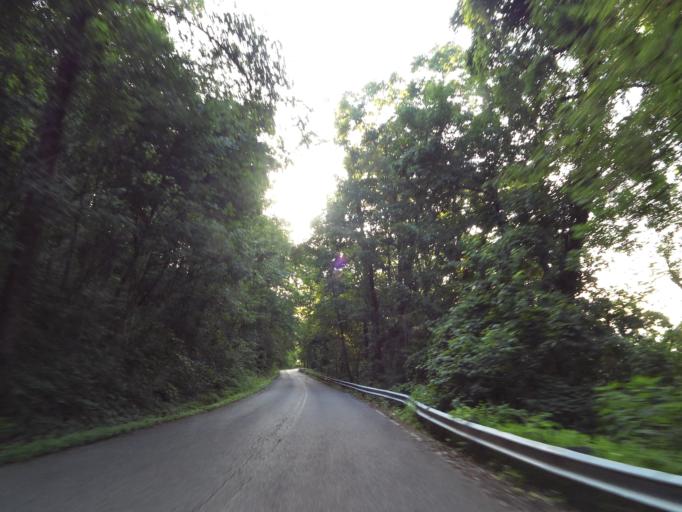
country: US
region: Tennessee
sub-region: Blount County
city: Maryville
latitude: 35.6309
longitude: -83.9489
